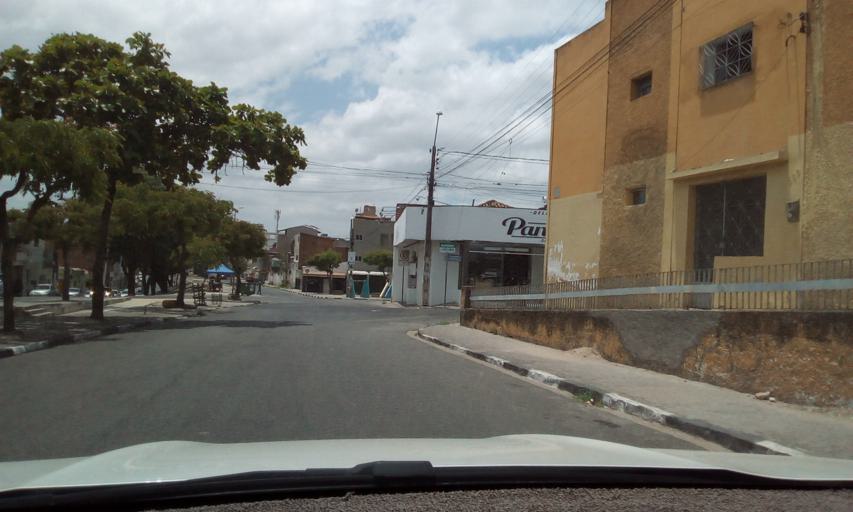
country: BR
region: Pernambuco
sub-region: Caruaru
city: Caruaru
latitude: -8.2785
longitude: -35.9755
